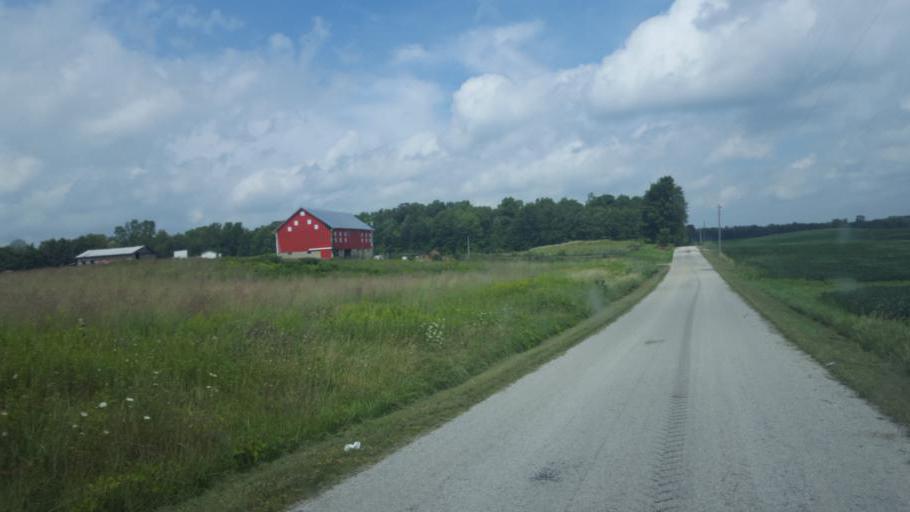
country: US
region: Ohio
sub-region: Crawford County
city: Galion
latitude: 40.6342
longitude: -82.7090
